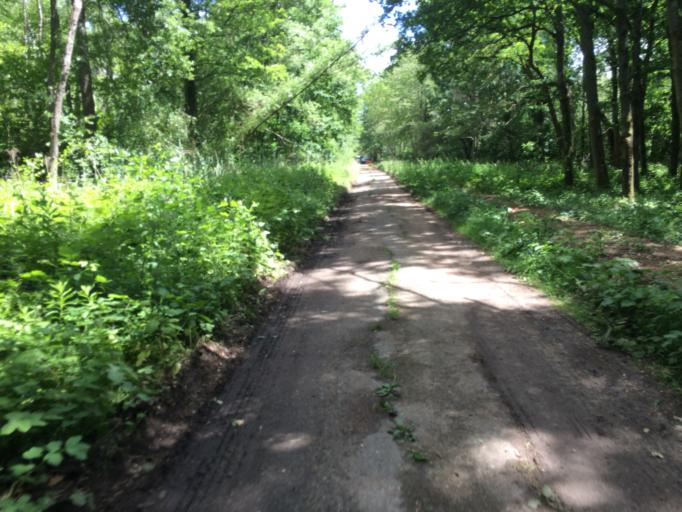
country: FR
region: Ile-de-France
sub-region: Departement de l'Essonne
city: Les Ulis
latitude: 48.6716
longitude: 2.1907
